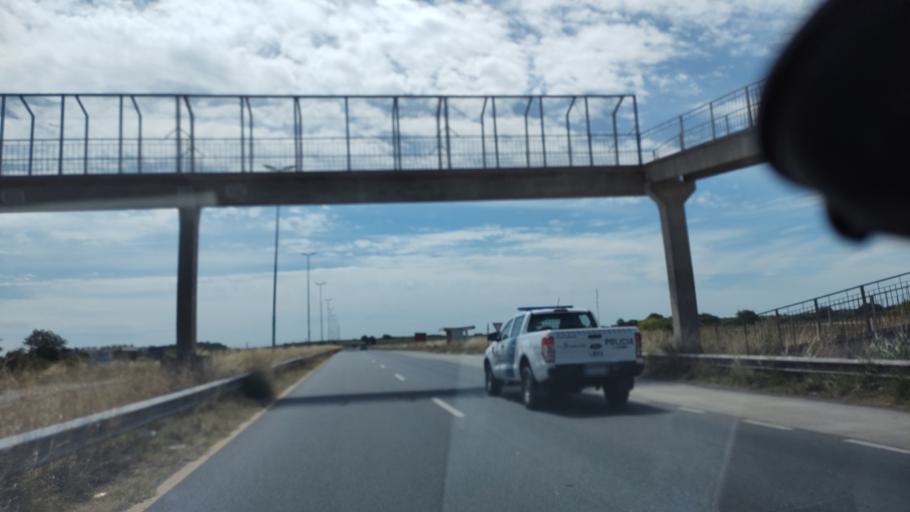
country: AR
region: Buenos Aires
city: Canuelas
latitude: -35.0253
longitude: -58.7353
